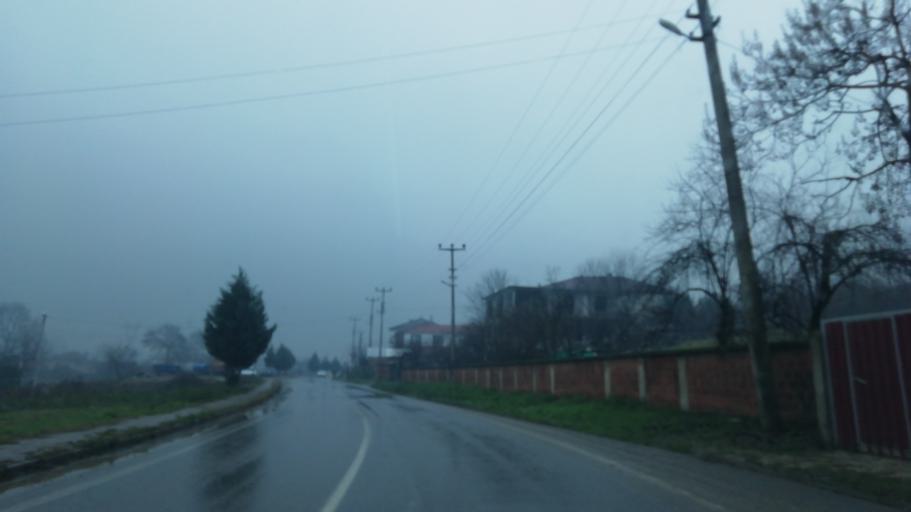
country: TR
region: Sakarya
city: Karapurcek
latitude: 40.6897
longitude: 30.4984
